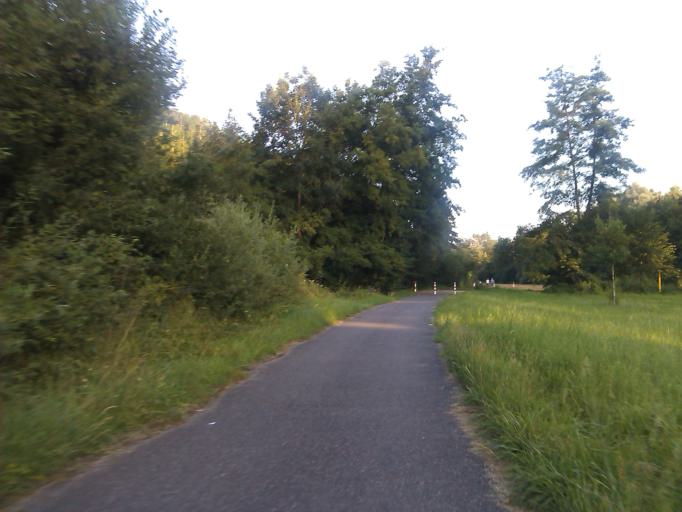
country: DE
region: Baden-Wuerttemberg
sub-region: Karlsruhe Region
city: Muhlhausen
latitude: 49.2435
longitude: 8.7556
